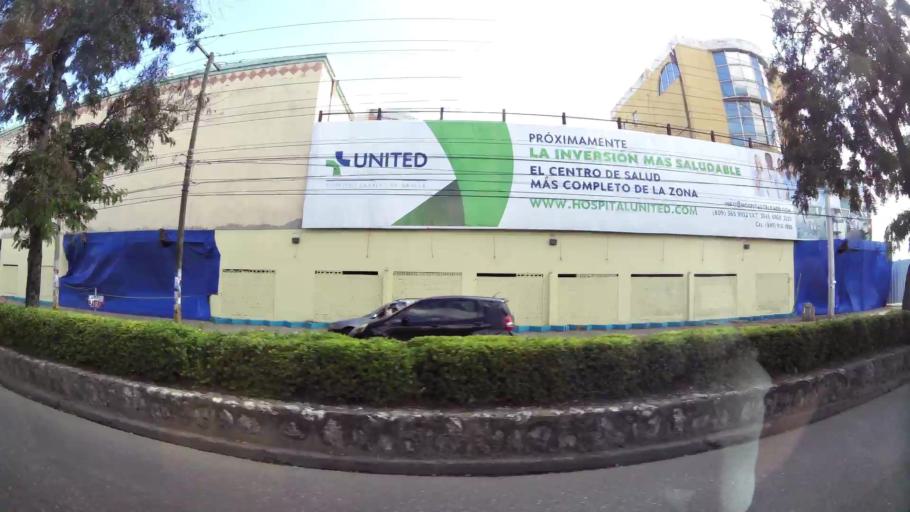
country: DO
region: Santo Domingo
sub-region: Santo Domingo
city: Santo Domingo Este
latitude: 18.5056
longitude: -69.8273
